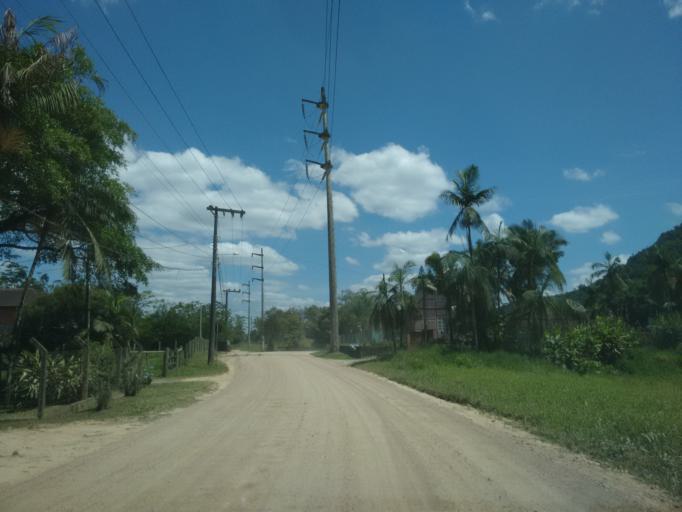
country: BR
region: Santa Catarina
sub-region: Pomerode
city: Pomerode
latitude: -26.7784
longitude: -49.1655
